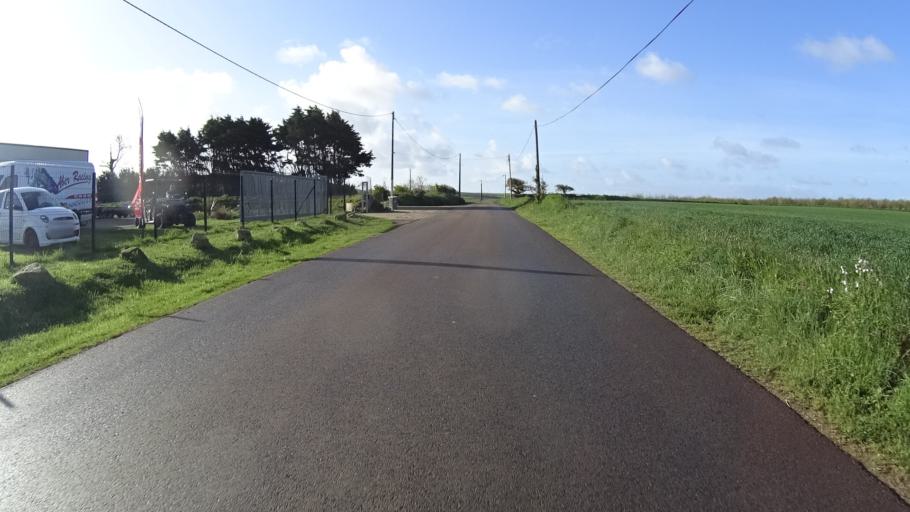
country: FR
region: Brittany
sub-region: Departement du Finistere
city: Plouarzel
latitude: 48.4313
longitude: -4.7149
